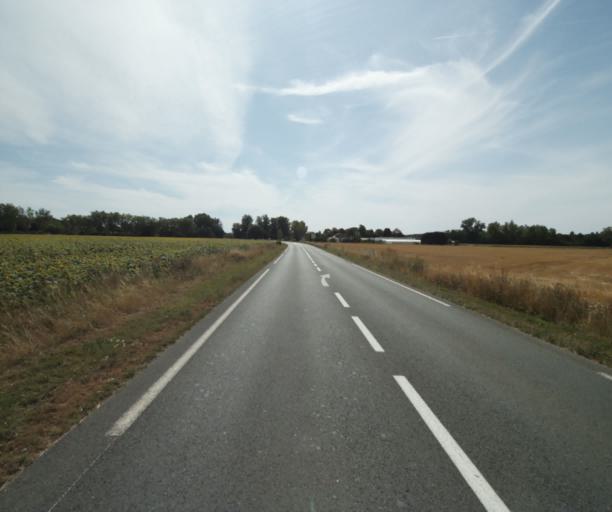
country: FR
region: Midi-Pyrenees
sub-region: Departement du Tarn
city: Soual
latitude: 43.5213
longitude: 2.0767
